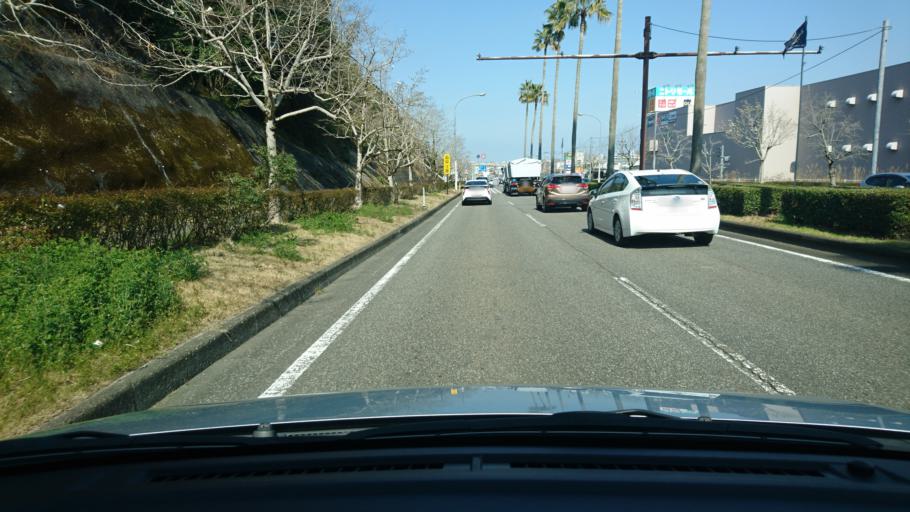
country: JP
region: Miyazaki
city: Miyazaki-shi
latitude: 31.8845
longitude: 131.4113
